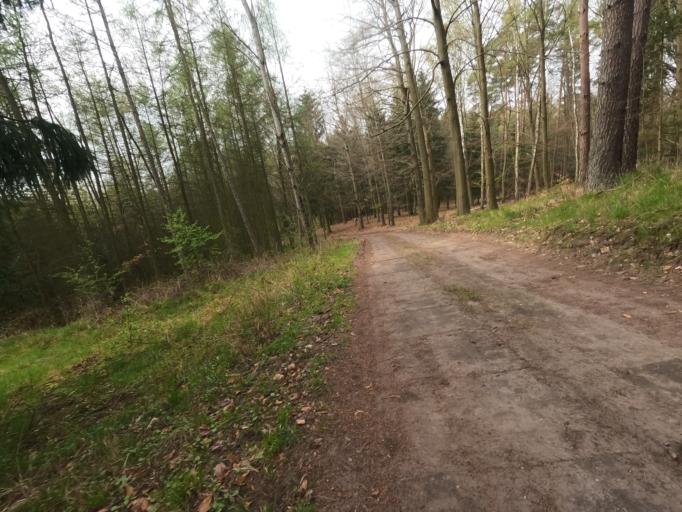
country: PL
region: West Pomeranian Voivodeship
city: Trzcinsko Zdroj
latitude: 52.9144
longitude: 14.5661
